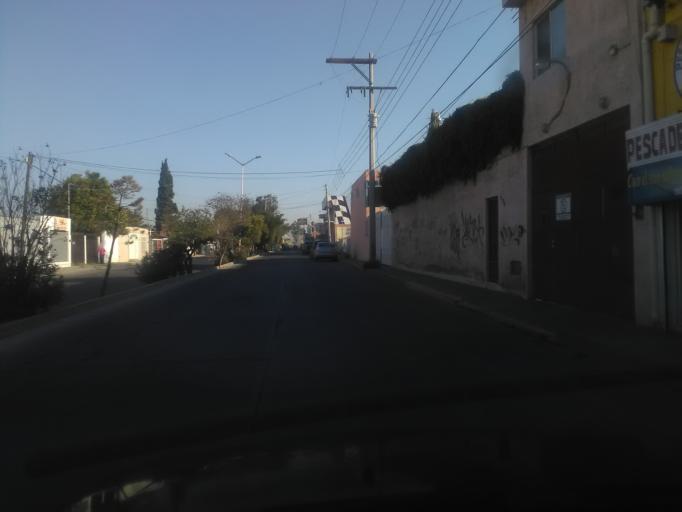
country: MX
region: Durango
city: Victoria de Durango
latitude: 24.0416
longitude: -104.6208
